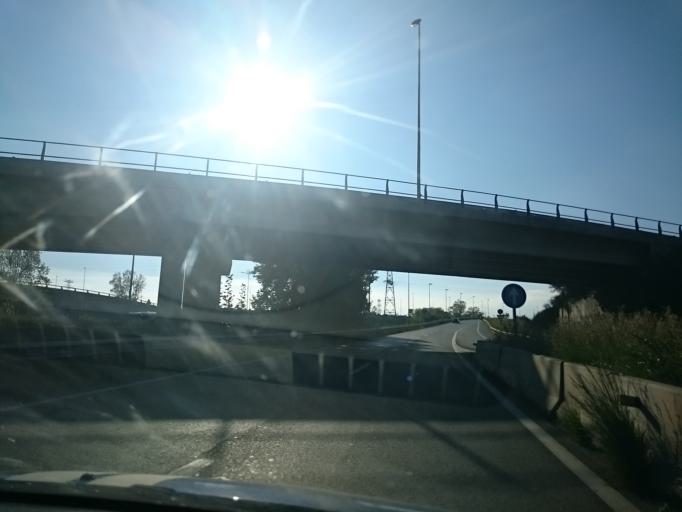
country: ES
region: Catalonia
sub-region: Provincia de Barcelona
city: L'Hospitalet de Llobregat
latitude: 41.3425
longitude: 2.1052
